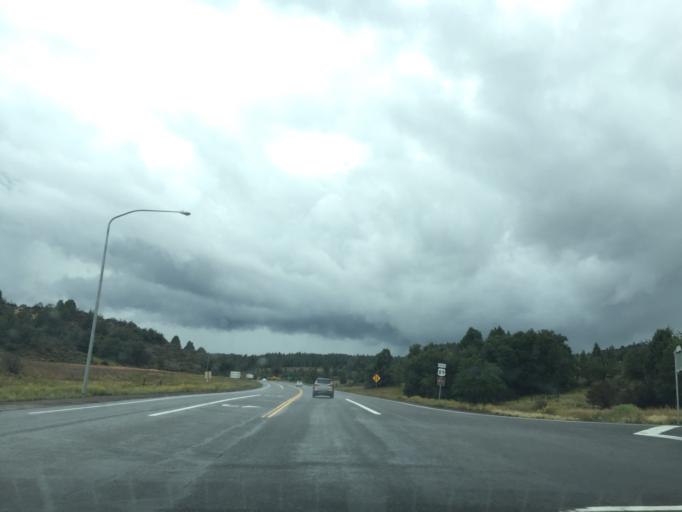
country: US
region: Utah
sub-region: Garfield County
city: Panguitch
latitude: 37.4889
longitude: -112.5125
